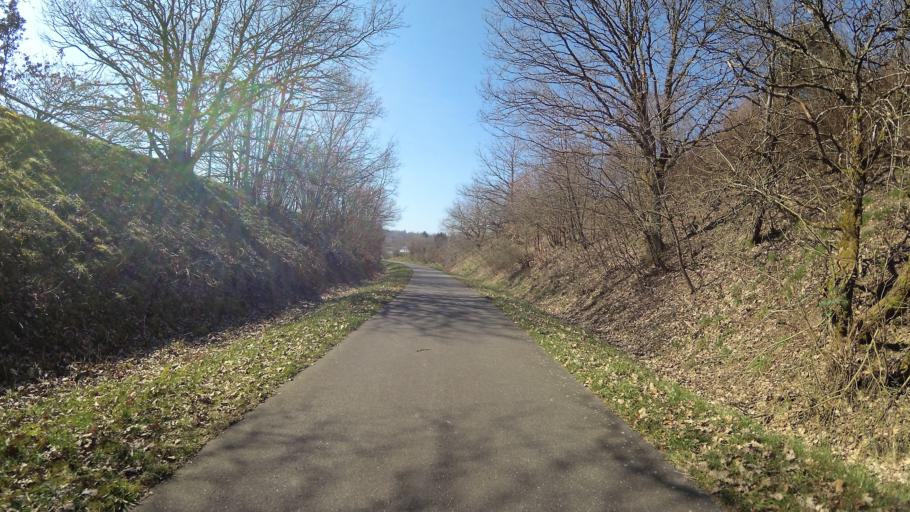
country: DE
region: Rheinland-Pfalz
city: Reinsfeld
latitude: 49.6787
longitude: 6.8842
